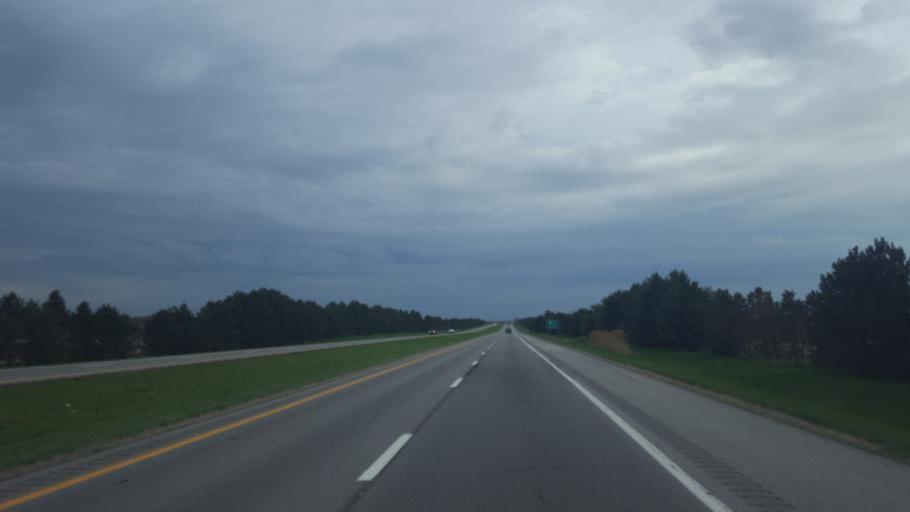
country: US
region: Ohio
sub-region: Wyandot County
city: Upper Sandusky
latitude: 40.8734
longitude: -83.3295
